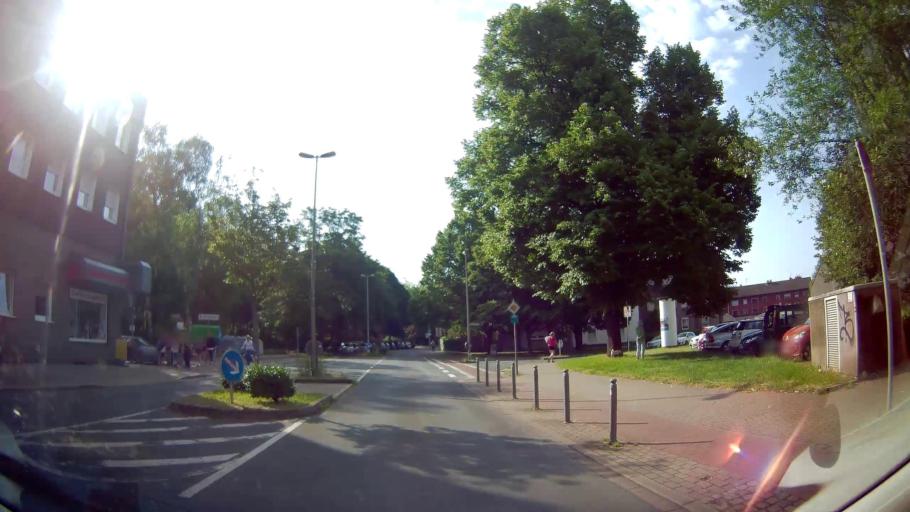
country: DE
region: North Rhine-Westphalia
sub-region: Regierungsbezirk Arnsberg
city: Herne
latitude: 51.5286
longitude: 7.2288
